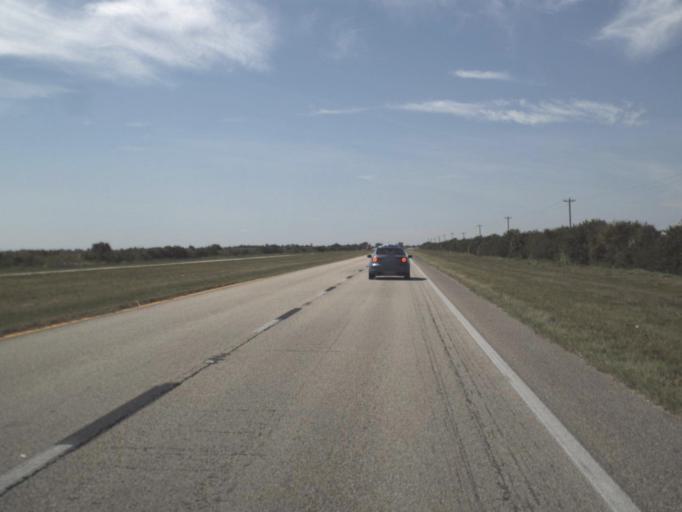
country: US
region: Florida
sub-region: Glades County
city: Moore Haven
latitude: 26.8338
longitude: -81.1740
